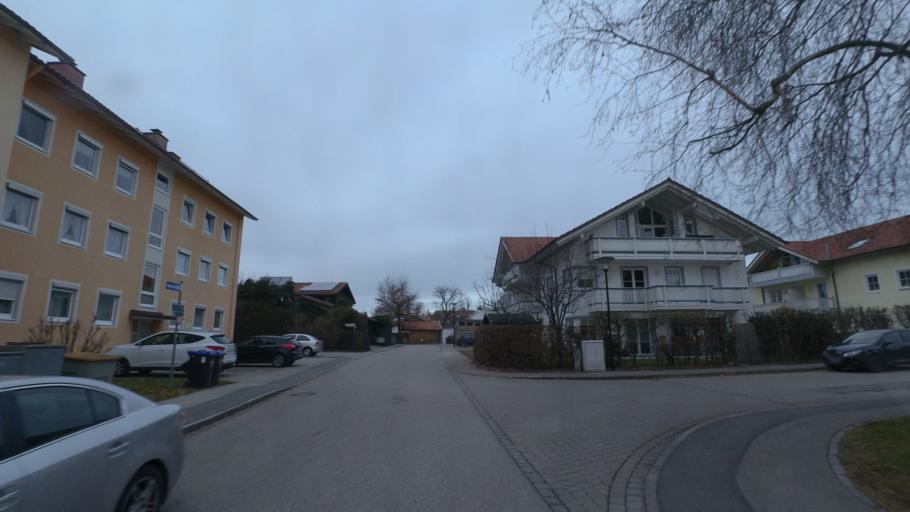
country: DE
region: Bavaria
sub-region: Upper Bavaria
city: Traunstein
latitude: 47.8701
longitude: 12.6290
